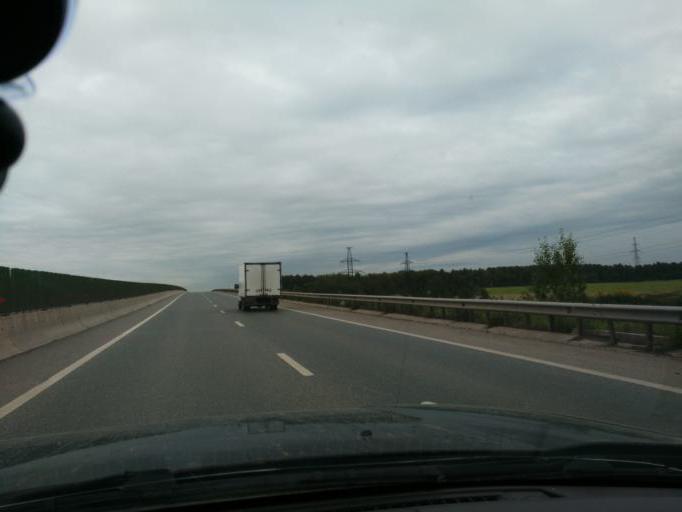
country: RU
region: Perm
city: Froly
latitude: 57.9317
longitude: 56.2871
